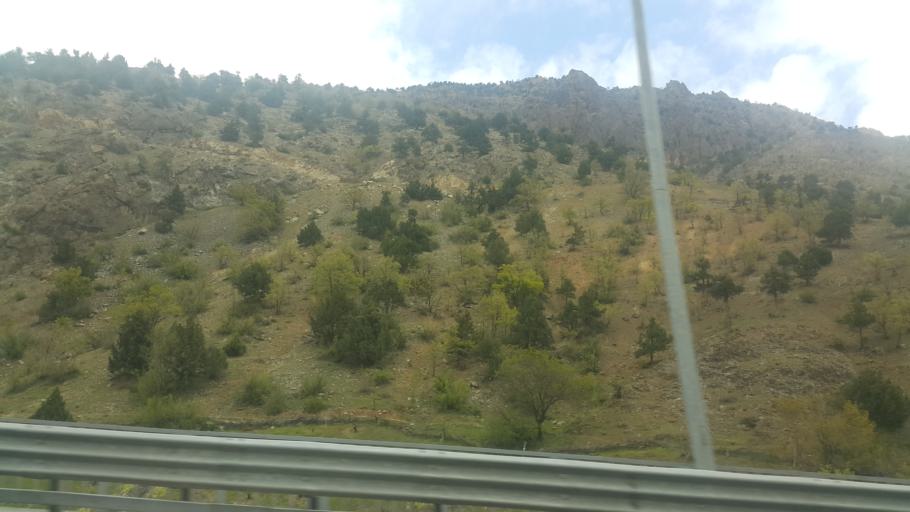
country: TR
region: Nigde
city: Ciftehan
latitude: 37.5340
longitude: 34.8035
